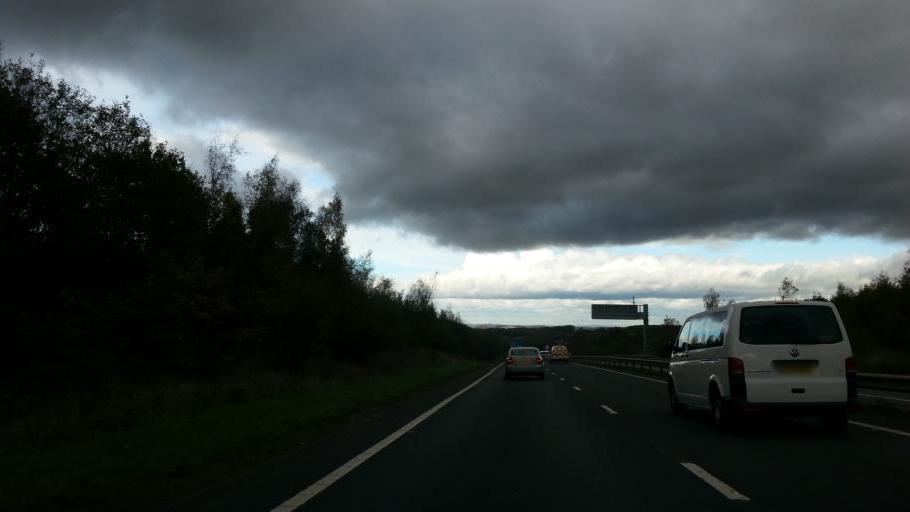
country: GB
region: England
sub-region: Leicestershire
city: Ashby de la Zouch
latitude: 52.7608
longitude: -1.4348
